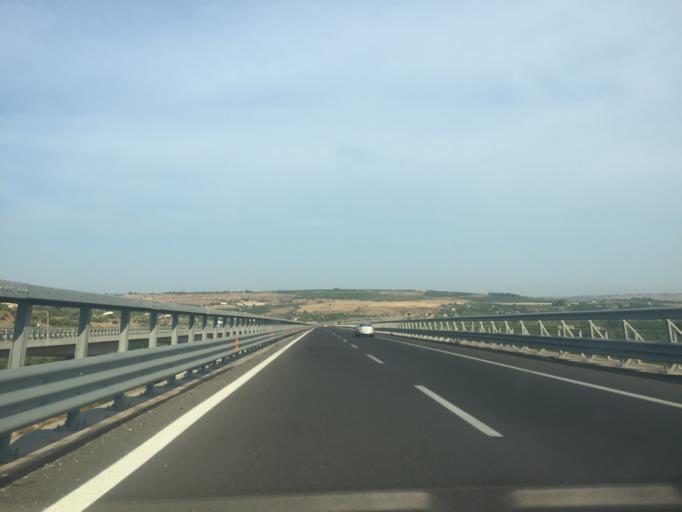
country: IT
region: Sicily
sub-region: Provincia di Siracusa
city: Villasmundo
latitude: 37.3018
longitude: 15.0736
